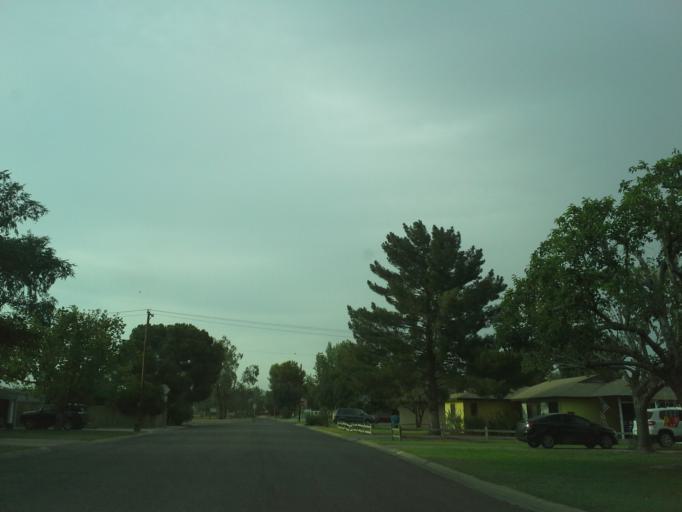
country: US
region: Arizona
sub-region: Maricopa County
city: Phoenix
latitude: 33.5266
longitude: -112.0868
